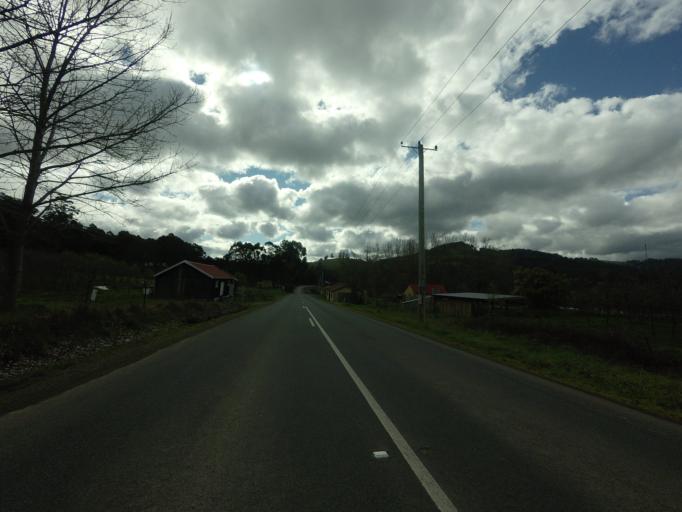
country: AU
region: Tasmania
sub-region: Huon Valley
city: Geeveston
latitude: -43.1713
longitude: 146.9436
